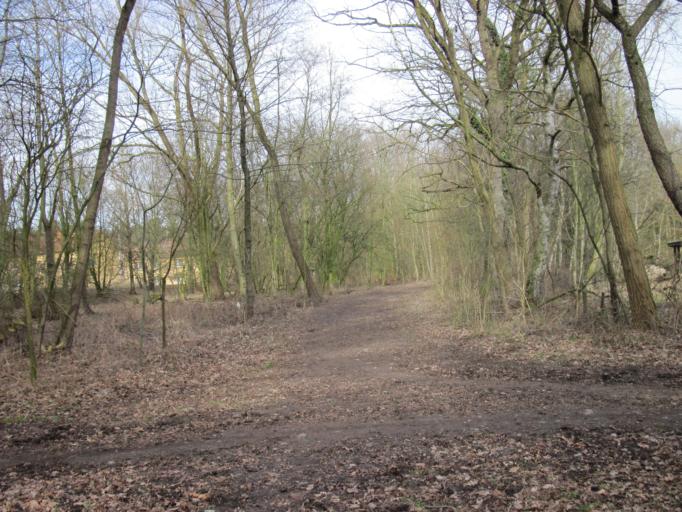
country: DE
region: North Rhine-Westphalia
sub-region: Regierungsbezirk Detmold
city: Paderborn
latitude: 51.7499
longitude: 8.7662
